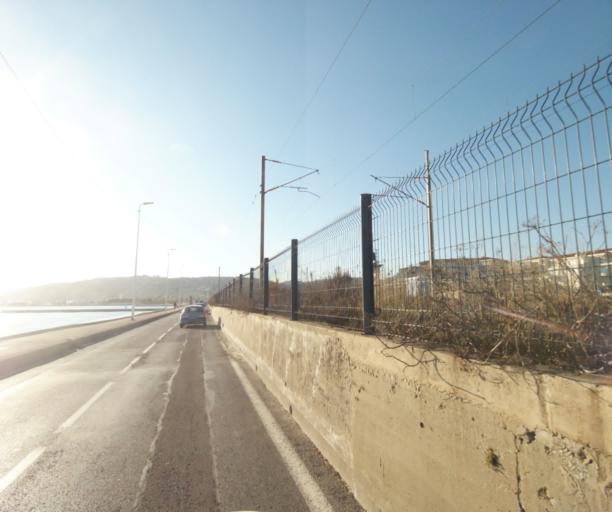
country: FR
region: Provence-Alpes-Cote d'Azur
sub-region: Departement des Alpes-Maritimes
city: Antibes
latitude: 43.5708
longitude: 7.0932
